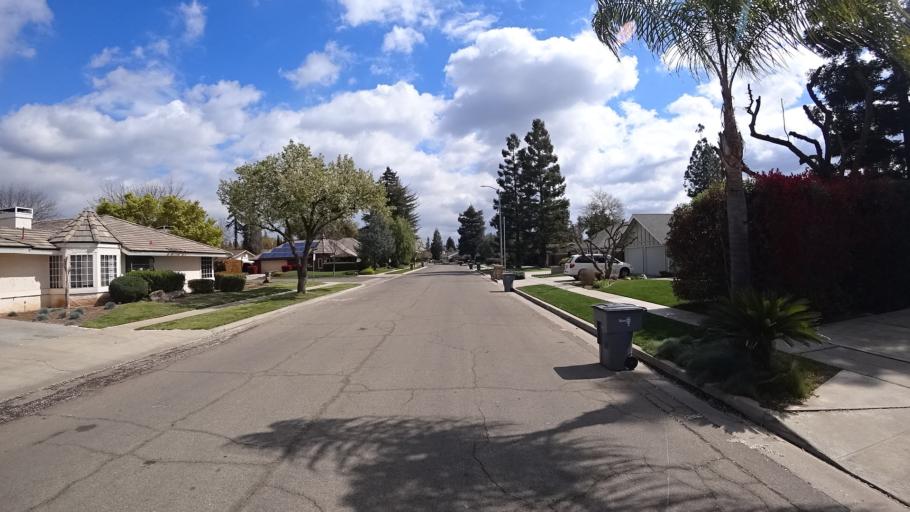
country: US
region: California
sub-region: Fresno County
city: Fresno
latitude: 36.8352
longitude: -119.8580
